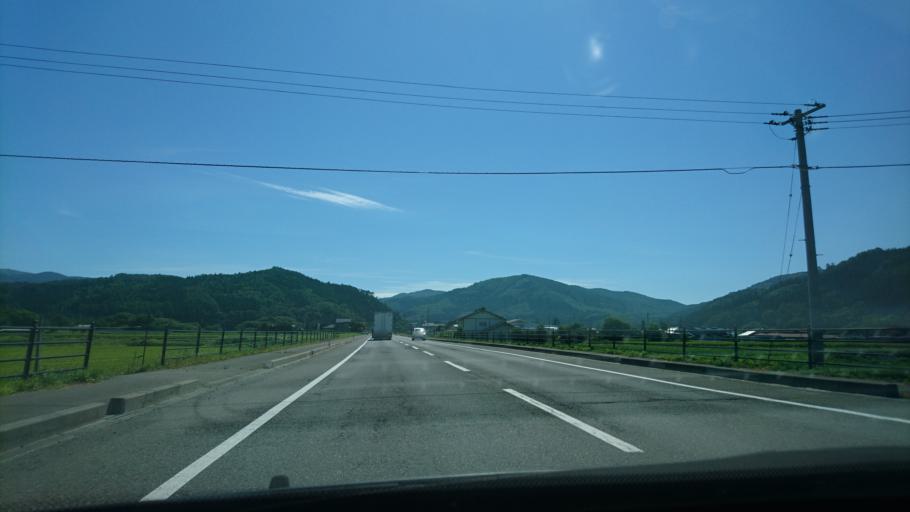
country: JP
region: Iwate
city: Tono
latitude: 39.2734
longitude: 141.5809
